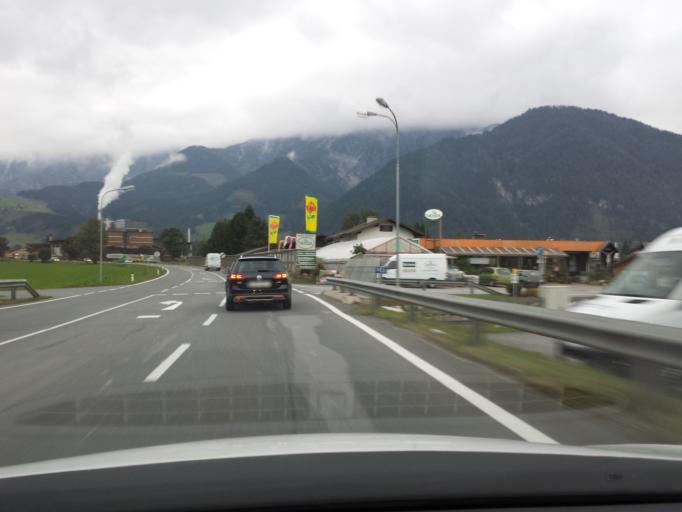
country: AT
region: Salzburg
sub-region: Politischer Bezirk Zell am See
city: Saalfelden am Steinernen Meer
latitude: 47.4389
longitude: 12.8199
